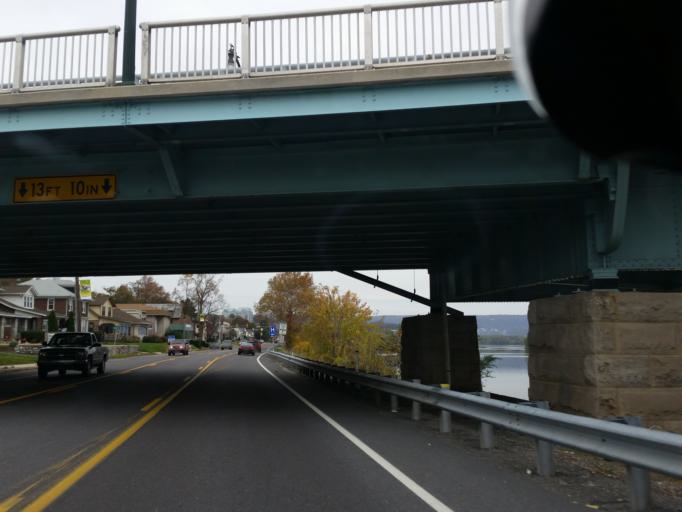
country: US
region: Pennsylvania
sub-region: Cumberland County
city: Wormleysburg
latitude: 40.2603
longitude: -76.9045
